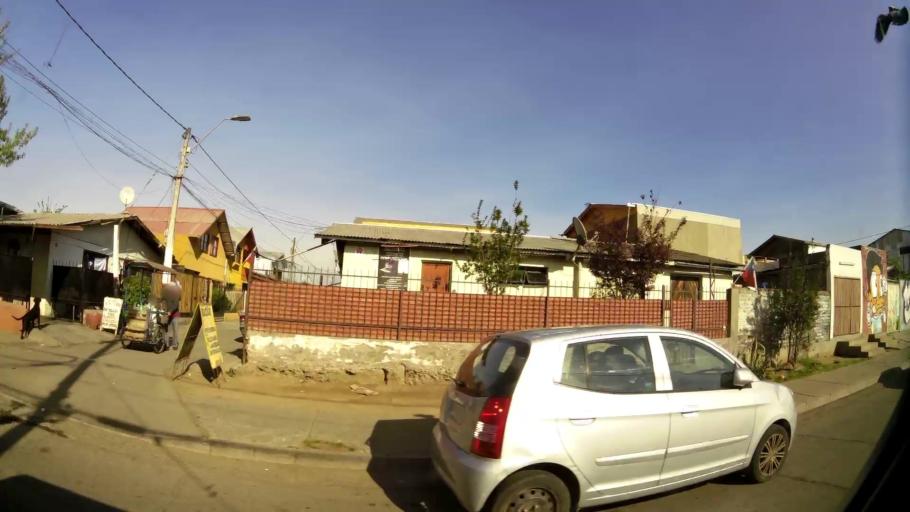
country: CL
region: Santiago Metropolitan
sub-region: Provincia de Santiago
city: Lo Prado
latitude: -33.4155
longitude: -70.7601
